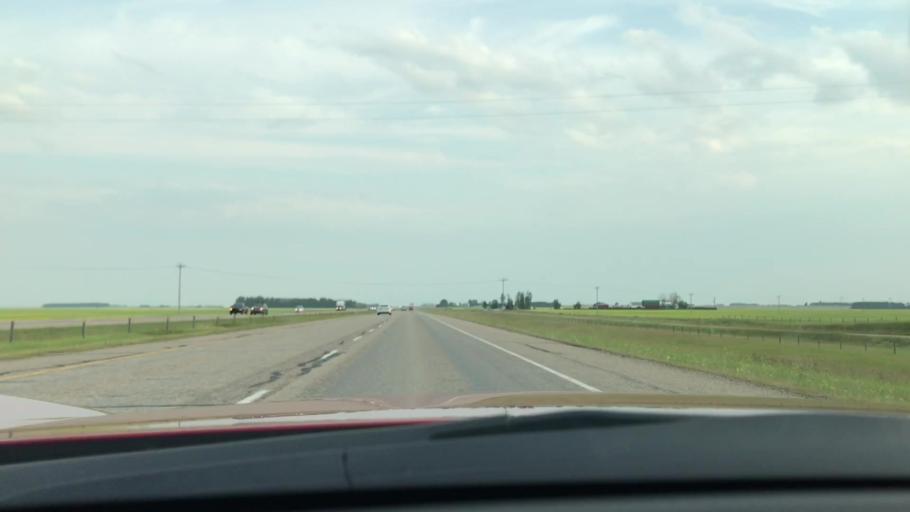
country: CA
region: Alberta
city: Olds
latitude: 51.8480
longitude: -114.0263
